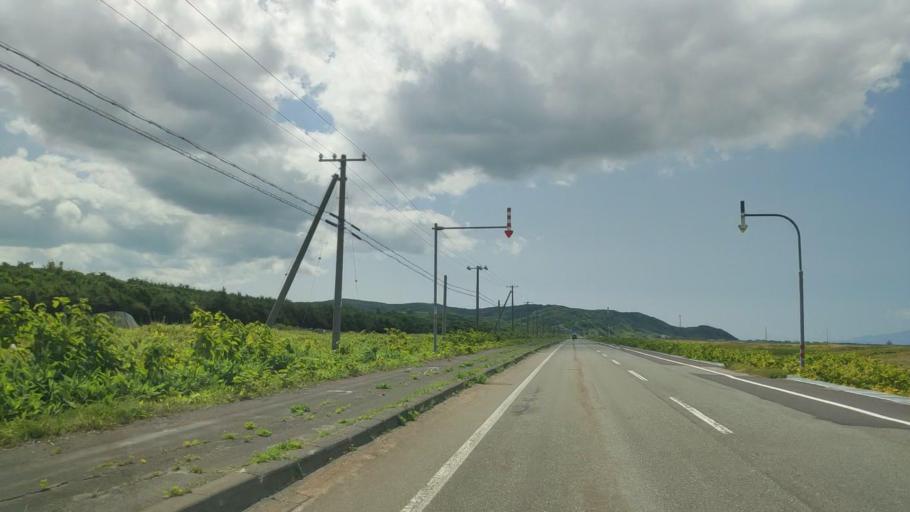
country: JP
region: Hokkaido
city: Wakkanai
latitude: 45.3235
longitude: 141.6413
